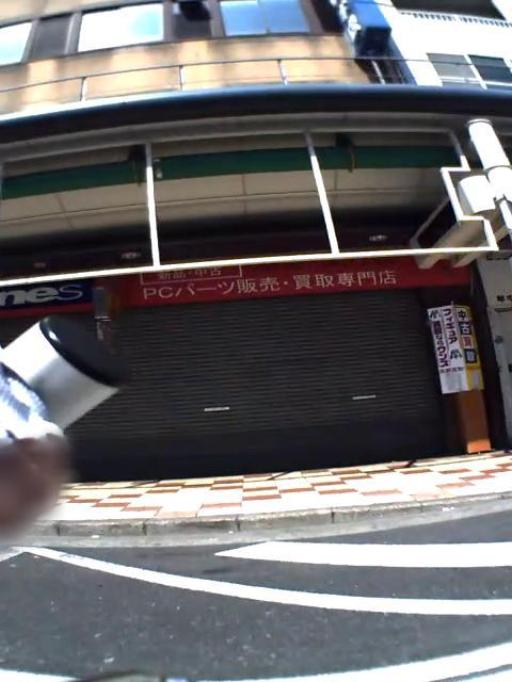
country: JP
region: Osaka
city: Osaka-shi
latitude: 34.6596
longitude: 135.5059
